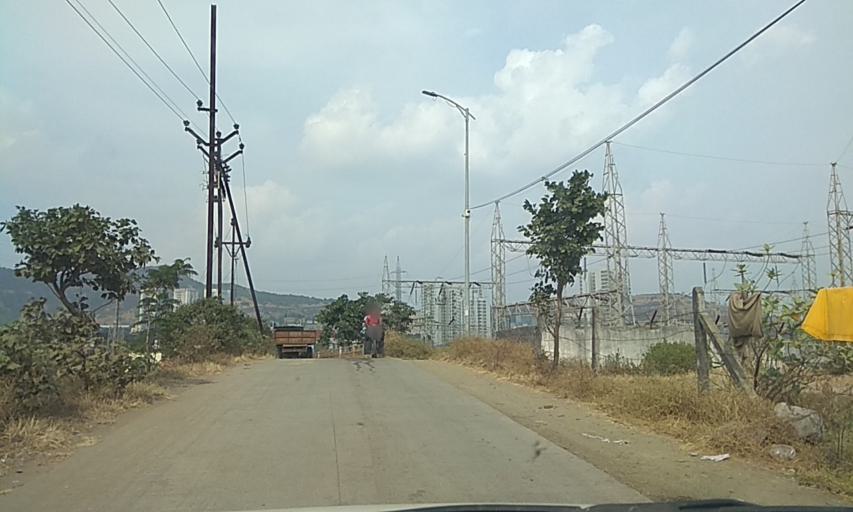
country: IN
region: Maharashtra
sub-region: Pune Division
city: Pimpri
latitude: 18.5868
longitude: 73.7059
